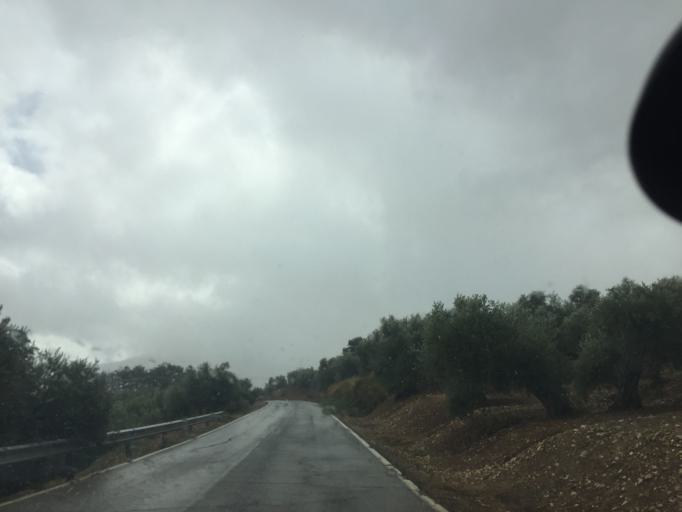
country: ES
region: Andalusia
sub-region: Provincia de Jaen
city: Jimena
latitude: 37.8179
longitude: -3.4643
